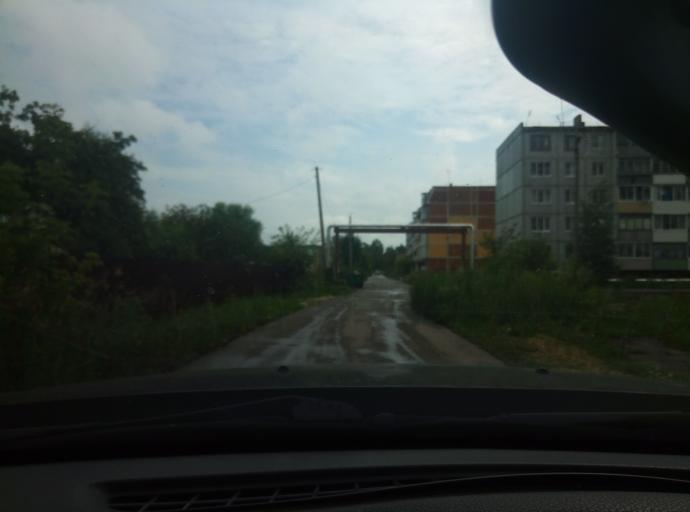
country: RU
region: Tula
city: Kimovsk
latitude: 53.9758
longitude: 38.5258
